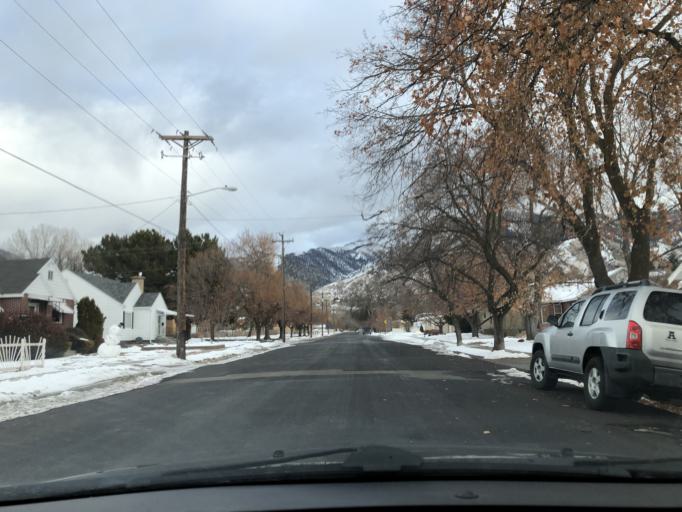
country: US
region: Utah
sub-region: Cache County
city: River Heights
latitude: 41.7293
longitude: -111.8218
